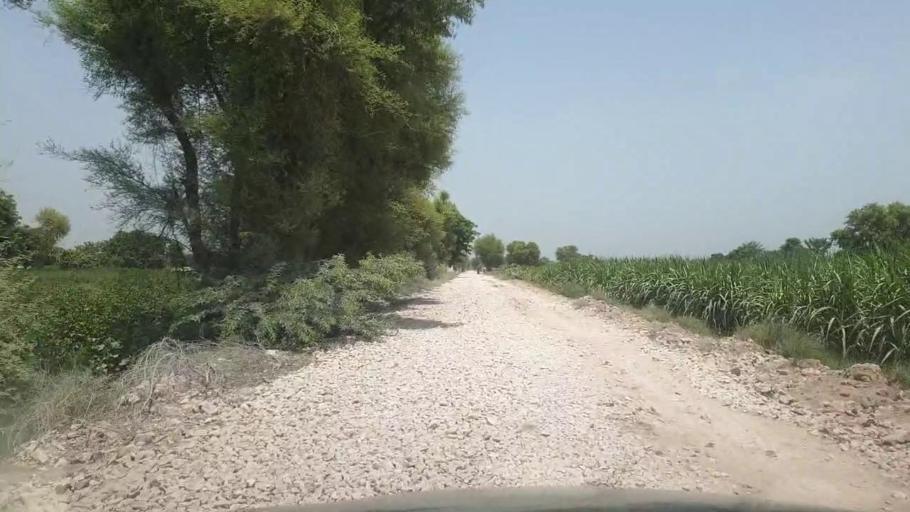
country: PK
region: Sindh
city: Sobhadero
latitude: 27.3254
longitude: 68.3511
